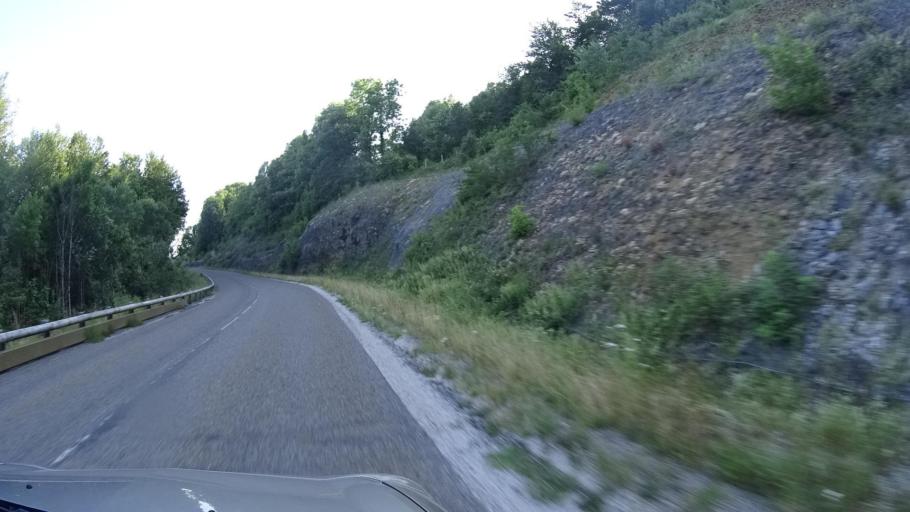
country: FR
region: Franche-Comte
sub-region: Departement du Jura
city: Longchaumois
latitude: 46.5124
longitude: 5.9584
